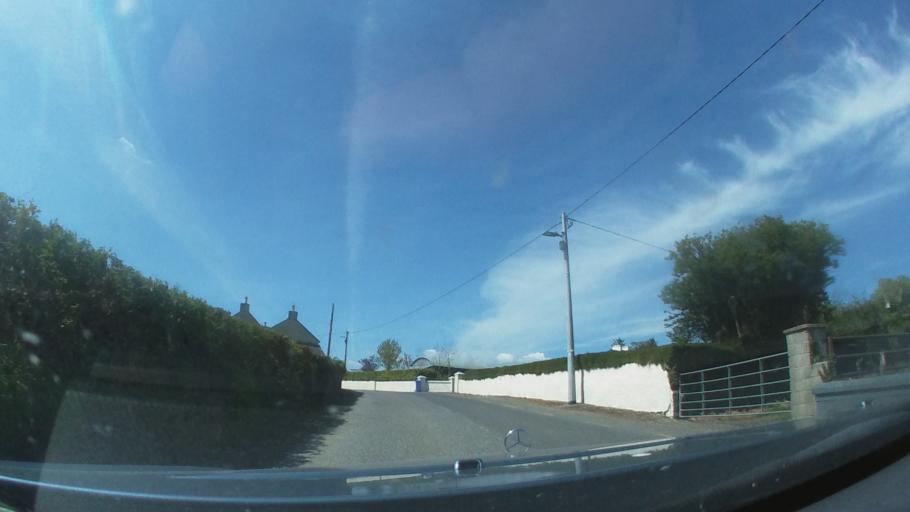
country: IE
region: Leinster
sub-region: Kilkenny
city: Callan
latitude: 52.6220
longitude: -7.4276
